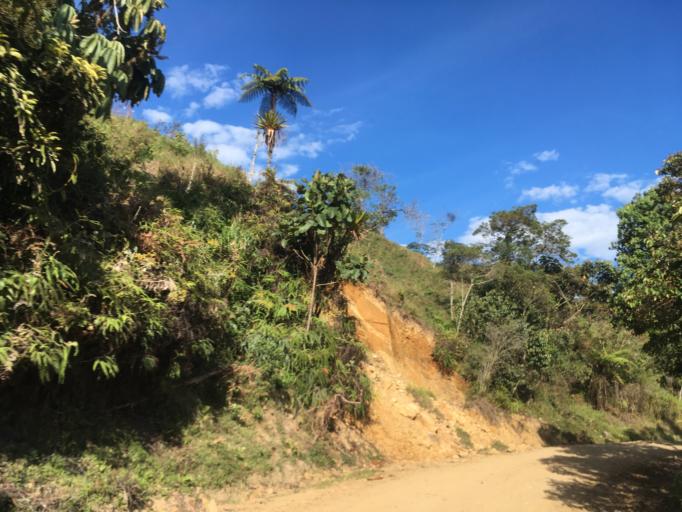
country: CO
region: Santander
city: Oiba
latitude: 6.1260
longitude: -73.1950
